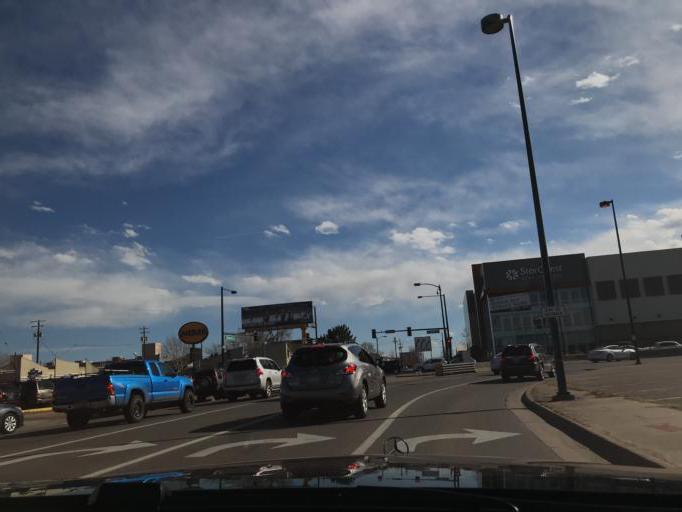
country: US
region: Colorado
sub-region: Denver County
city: Denver
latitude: 39.7264
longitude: -105.0003
